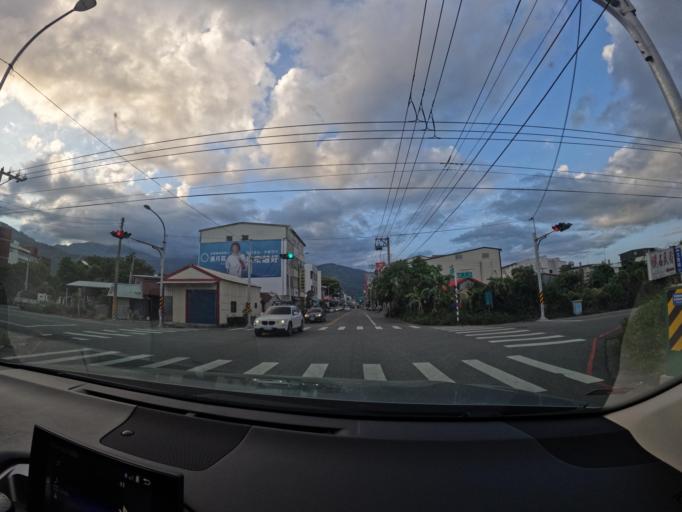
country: TW
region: Taiwan
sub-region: Taitung
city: Taitung
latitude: 23.3268
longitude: 121.3174
